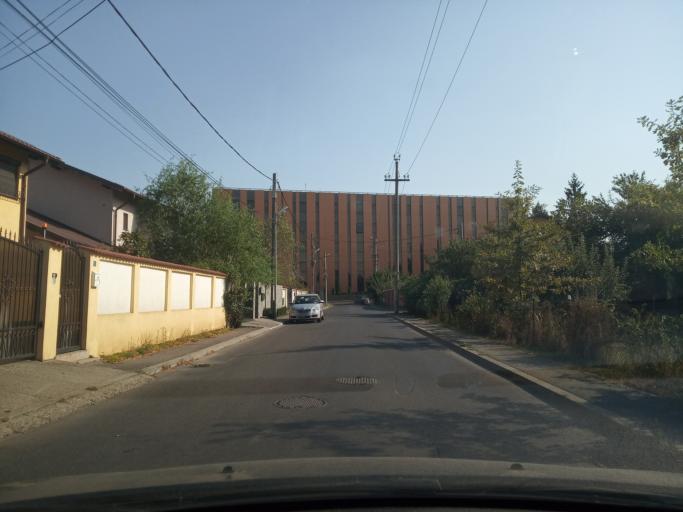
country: RO
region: Ilfov
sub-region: Comuna Corbeanca
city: Corbeanca
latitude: 44.6043
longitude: 26.0746
